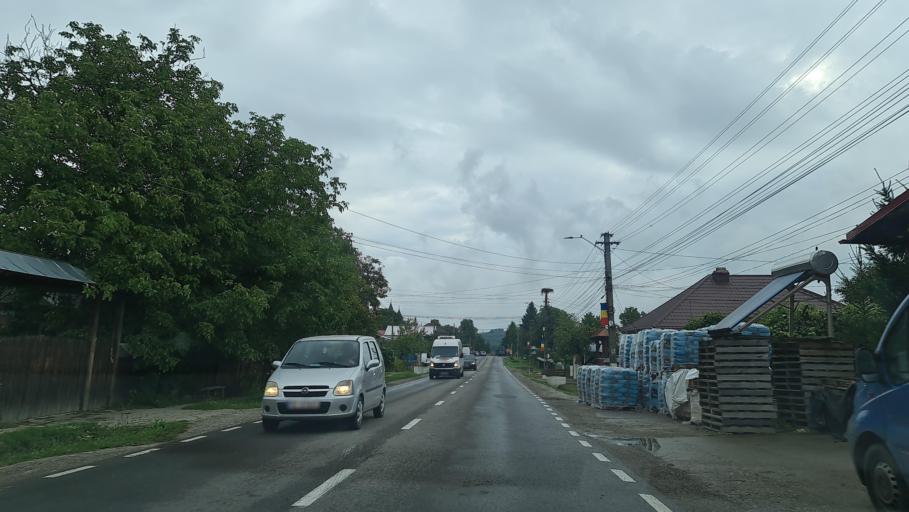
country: RO
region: Neamt
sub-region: Comuna Borlesti
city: Mastacan
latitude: 46.7765
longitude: 26.5016
